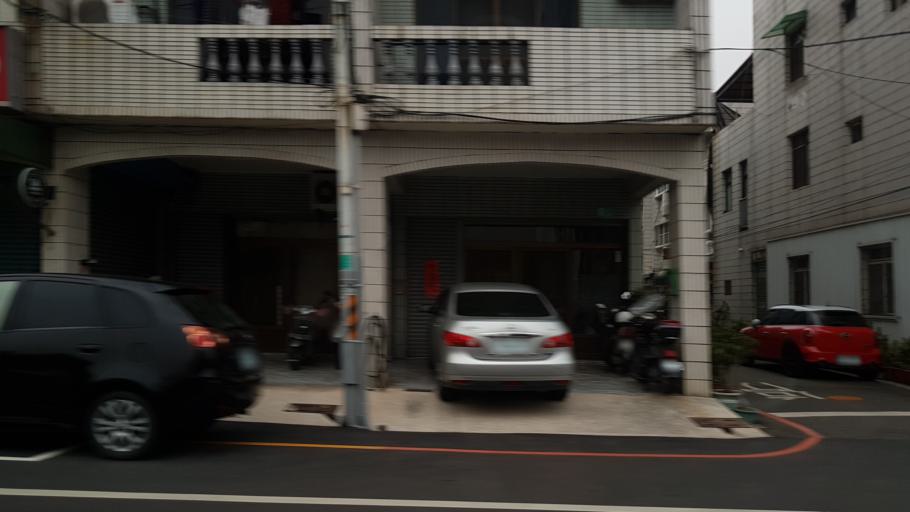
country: TW
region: Taiwan
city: Xinying
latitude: 23.3194
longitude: 120.3163
